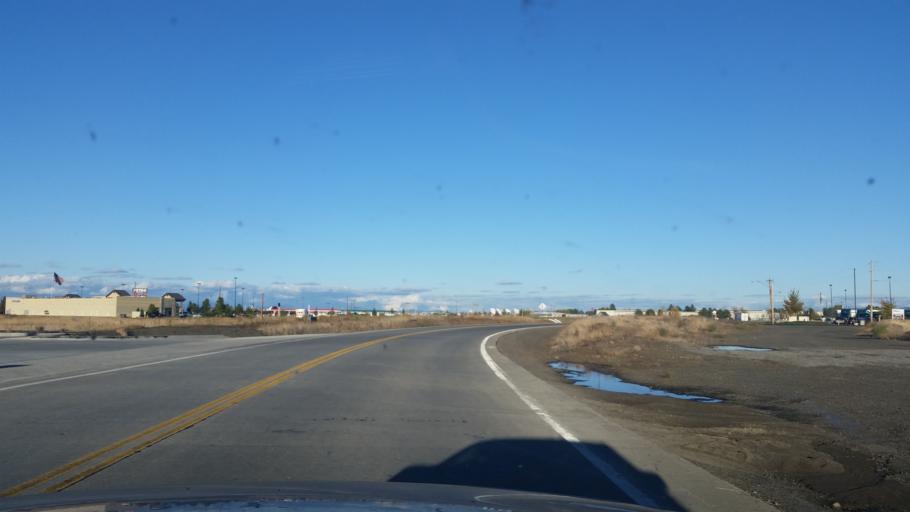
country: US
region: Washington
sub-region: Spokane County
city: Airway Heights
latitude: 47.5872
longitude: -117.5662
